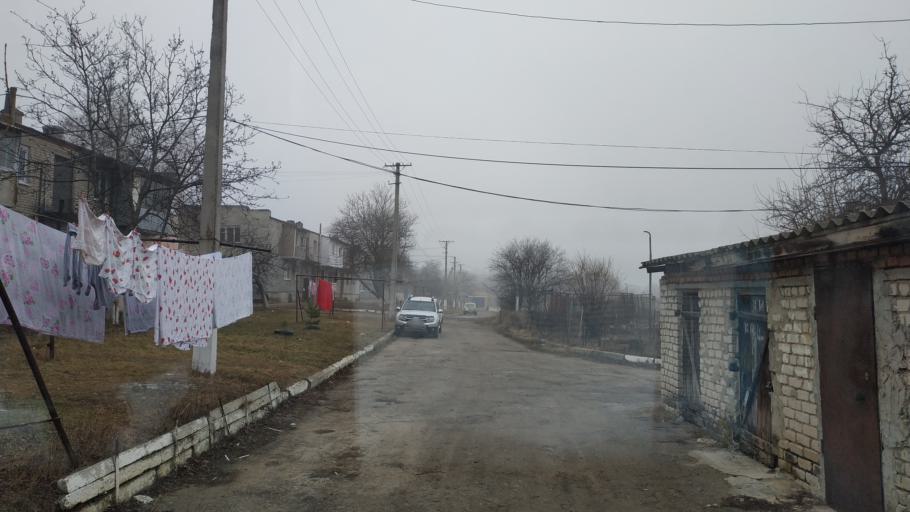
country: MD
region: Laloveni
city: Ialoveni
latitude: 46.9533
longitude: 28.6986
